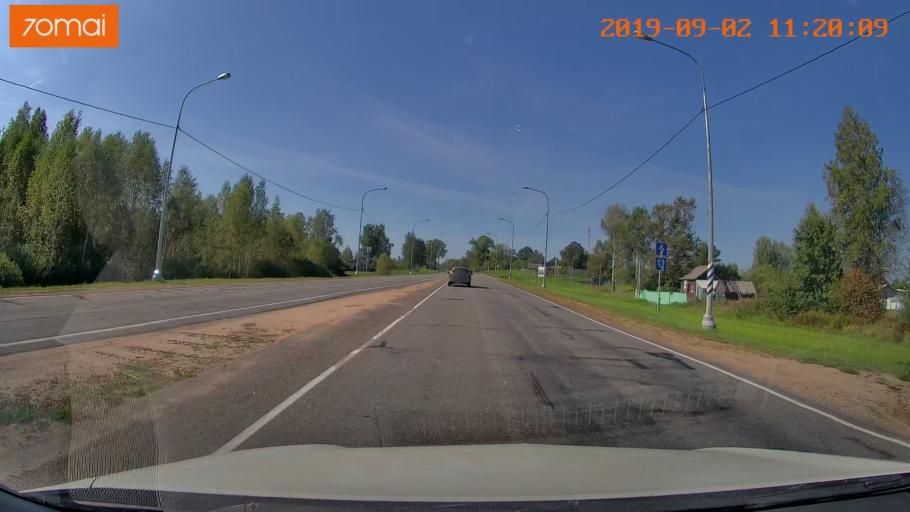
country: RU
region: Smolensk
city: Roslavl'
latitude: 54.0432
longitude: 33.0576
